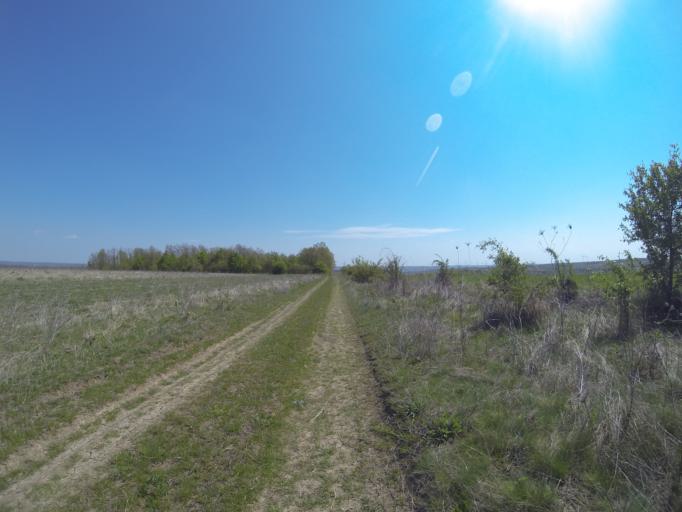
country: RO
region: Dolj
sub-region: Comuna Melinesti
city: Melinesti
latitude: 44.5478
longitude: 23.6554
